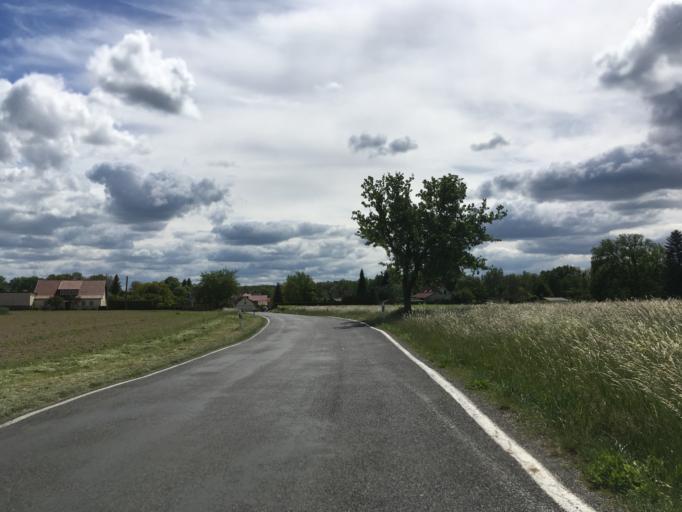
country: DE
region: Brandenburg
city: Protzel
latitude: 52.6903
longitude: 14.0108
